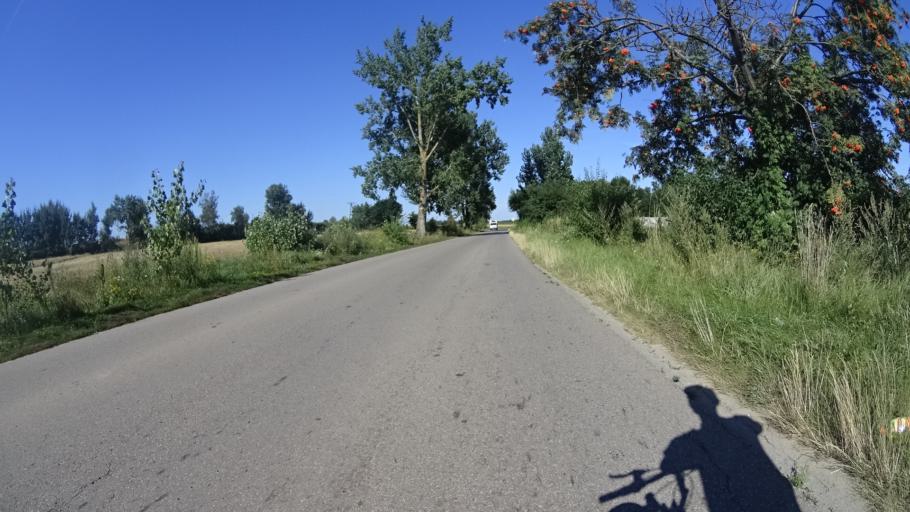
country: PL
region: Masovian Voivodeship
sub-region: Powiat bialobrzeski
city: Wysmierzyce
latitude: 51.6602
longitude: 20.8292
